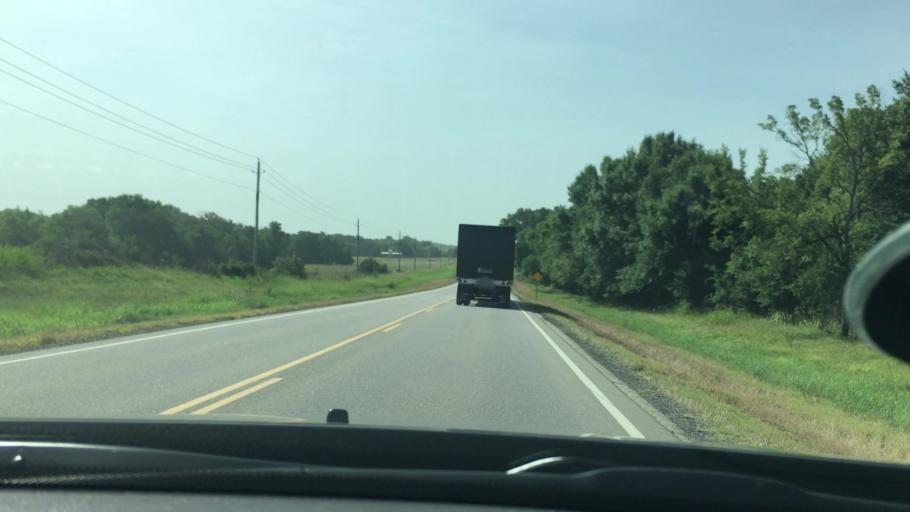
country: US
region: Oklahoma
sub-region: Atoka County
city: Atoka
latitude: 34.4132
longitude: -96.1849
